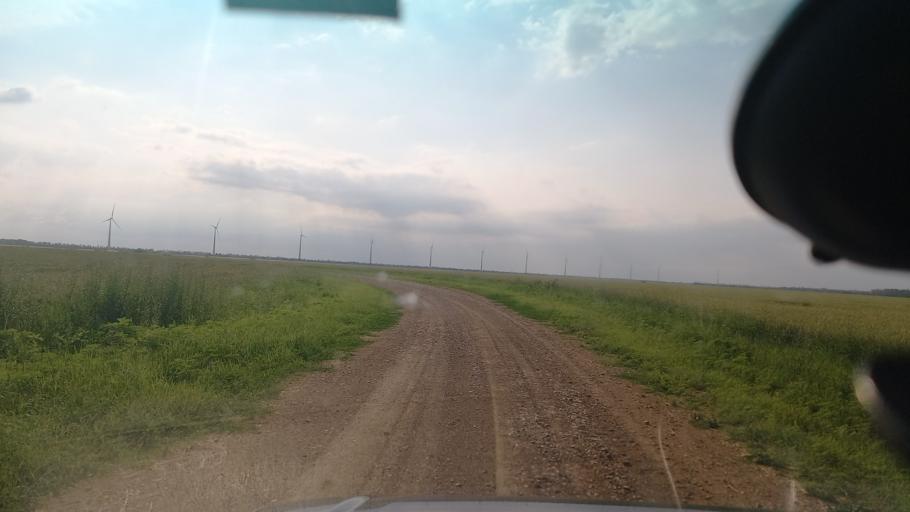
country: RU
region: Adygeya
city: Giaginskaya
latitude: 44.9555
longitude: 40.1004
